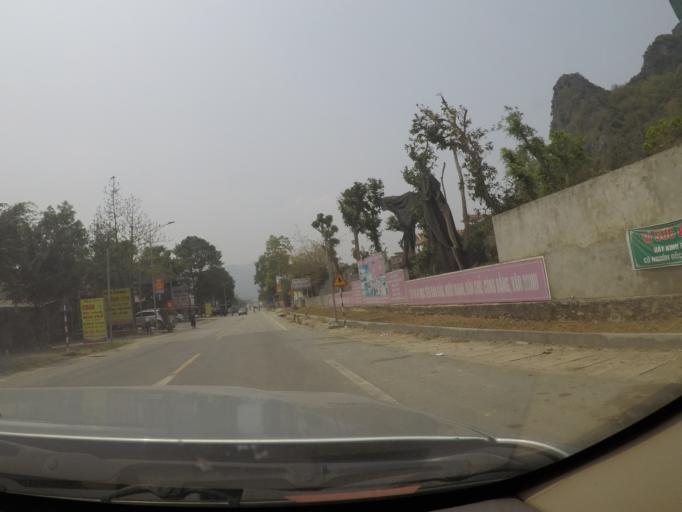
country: VN
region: Thanh Hoa
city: Thi Tran Cam Thuy
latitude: 20.2156
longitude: 105.4854
